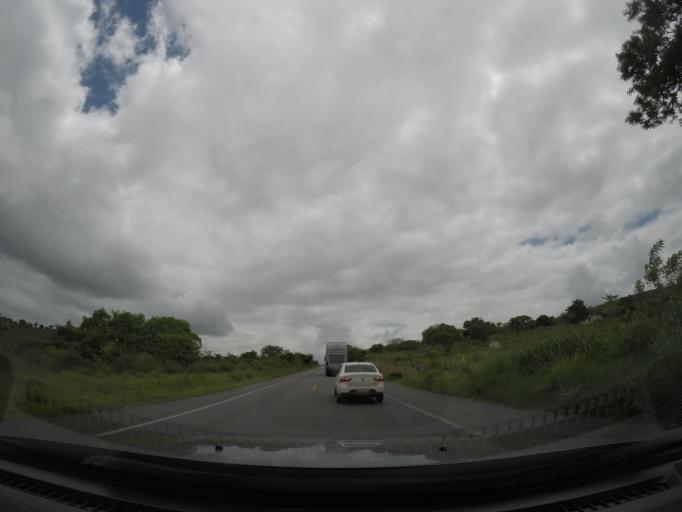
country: BR
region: Bahia
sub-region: Ruy Barbosa
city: Terra Nova
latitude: -12.4498
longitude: -40.6119
